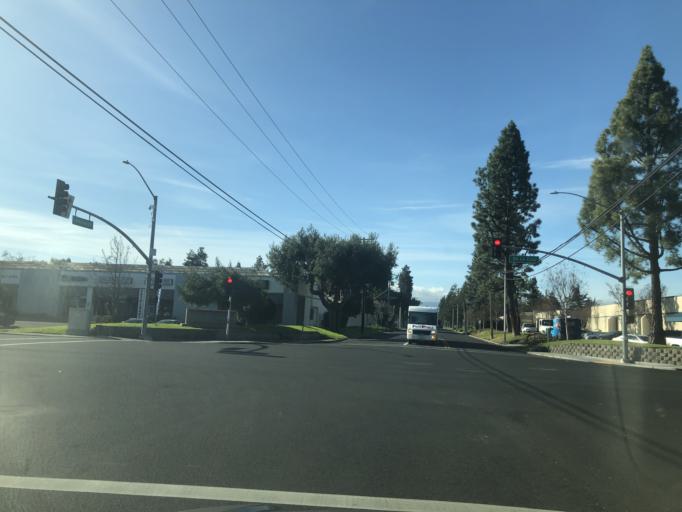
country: US
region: California
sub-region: Santa Clara County
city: Santa Clara
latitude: 37.3822
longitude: -121.9411
